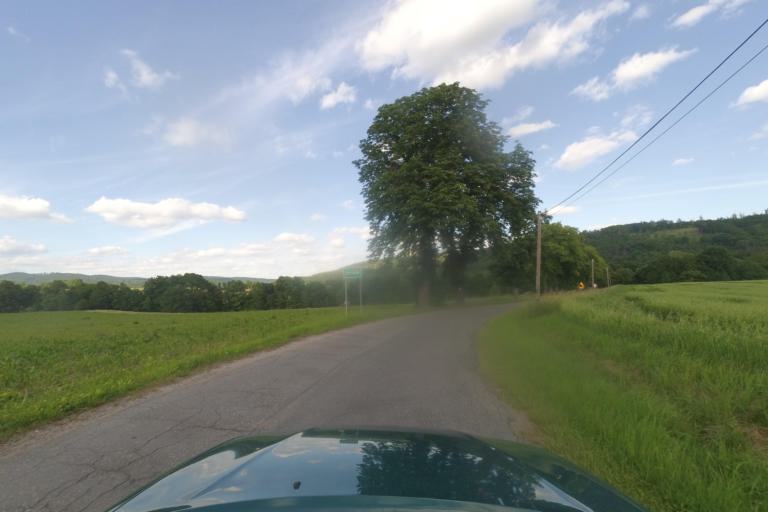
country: PL
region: Lower Silesian Voivodeship
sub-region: Powiat klodzki
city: Klodzko
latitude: 50.4827
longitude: 16.6731
